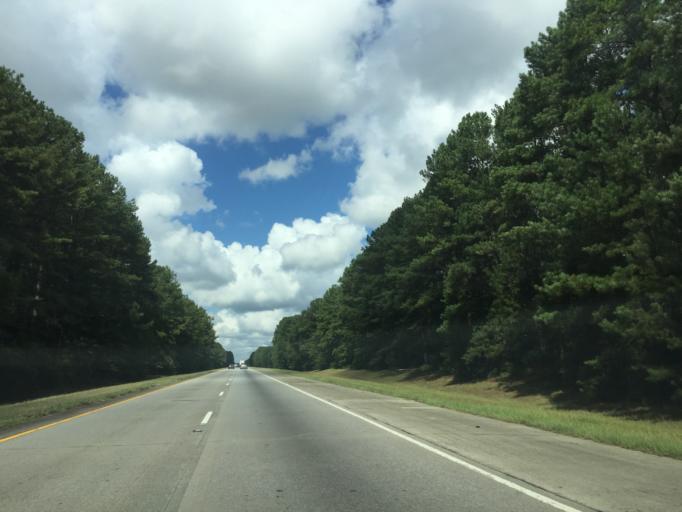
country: US
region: Georgia
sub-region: Candler County
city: Metter
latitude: 32.3857
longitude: -82.2504
